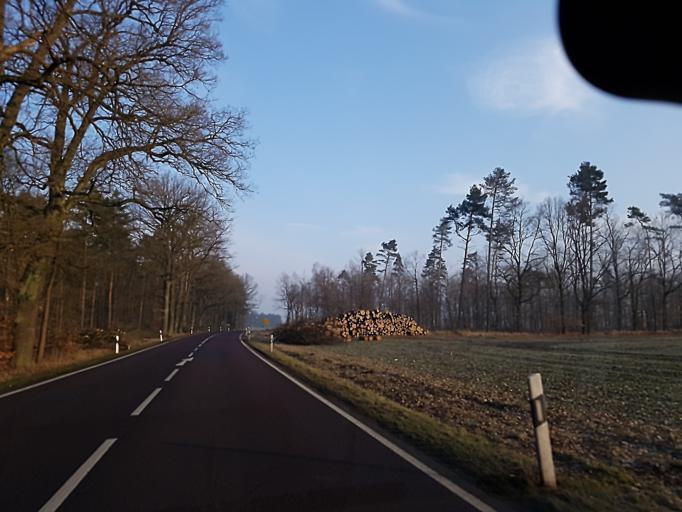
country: DE
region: Brandenburg
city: Wiesenburg
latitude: 52.0688
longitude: 12.4512
